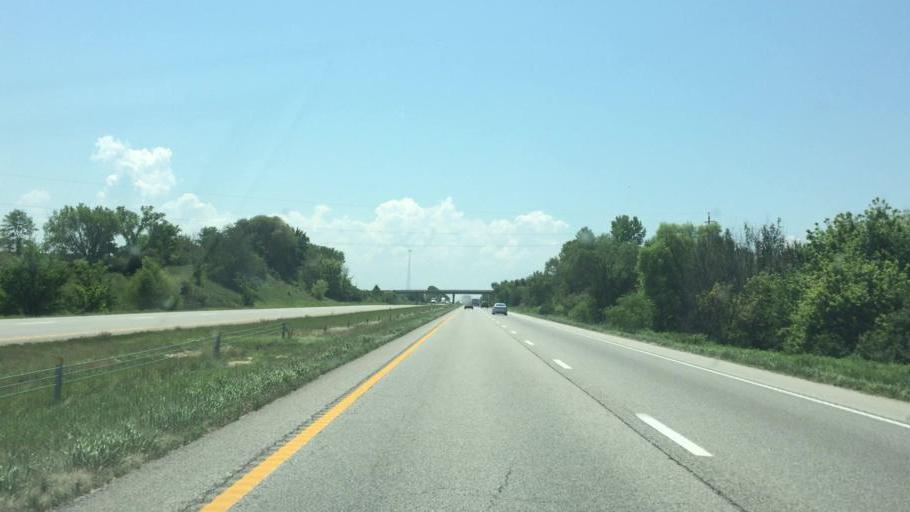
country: US
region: Missouri
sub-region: Platte County
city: Weston
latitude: 39.5602
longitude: -94.7883
